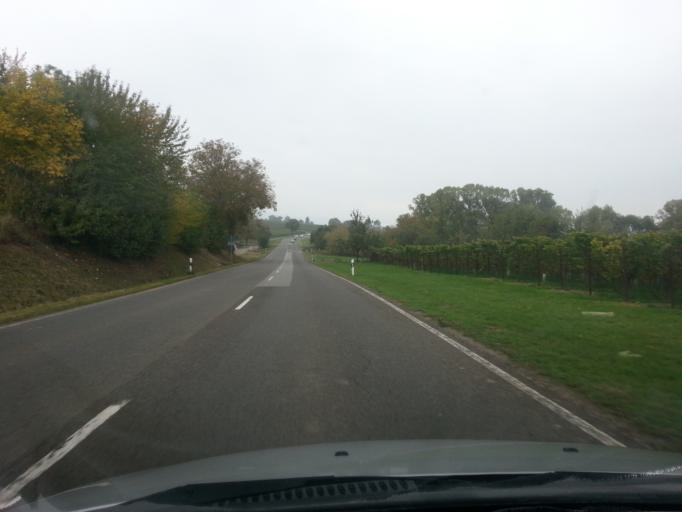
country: DE
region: Rheinland-Pfalz
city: Walsheim
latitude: 49.2259
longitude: 8.1317
